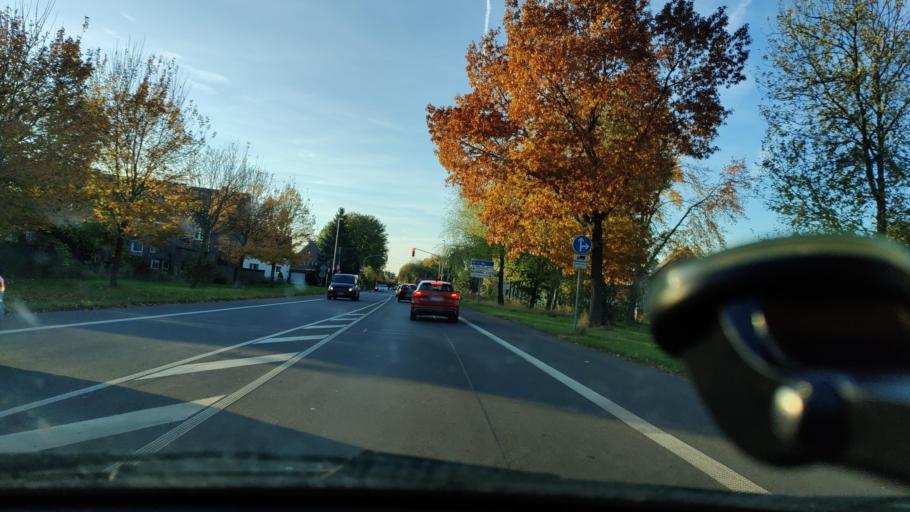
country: DE
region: North Rhine-Westphalia
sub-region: Regierungsbezirk Dusseldorf
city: Korschenbroich
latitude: 51.2271
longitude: 6.4747
